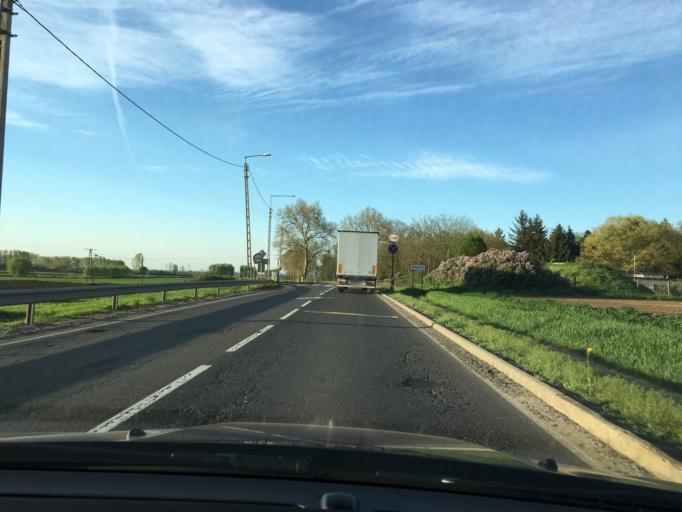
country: HU
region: Hajdu-Bihar
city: Mikepercs
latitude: 47.4281
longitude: 21.6258
